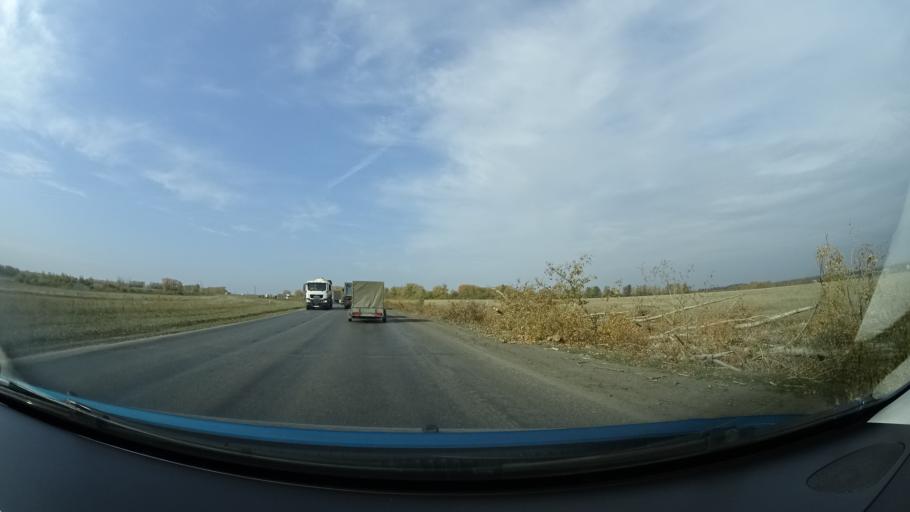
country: RU
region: Bashkortostan
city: Buzdyak
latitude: 54.6264
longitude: 54.4459
